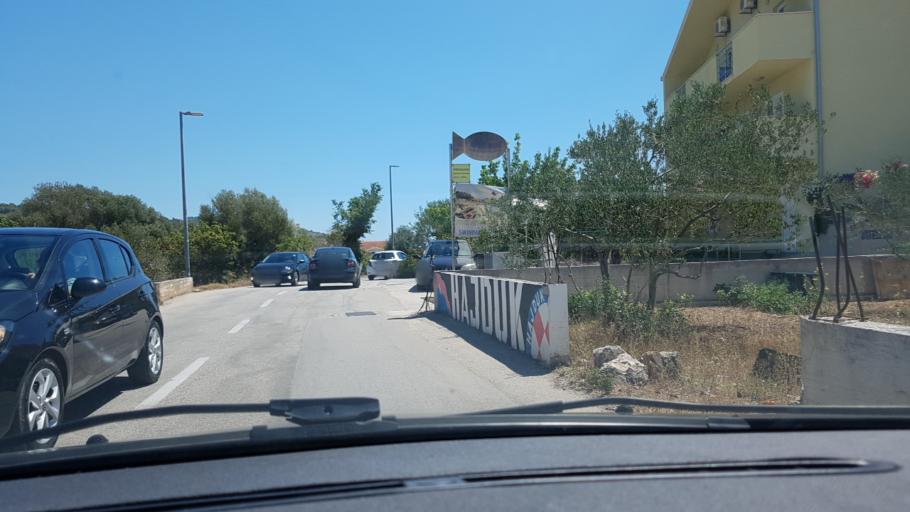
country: HR
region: Splitsko-Dalmatinska
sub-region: Grad Trogir
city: Trogir
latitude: 43.4922
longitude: 16.2662
